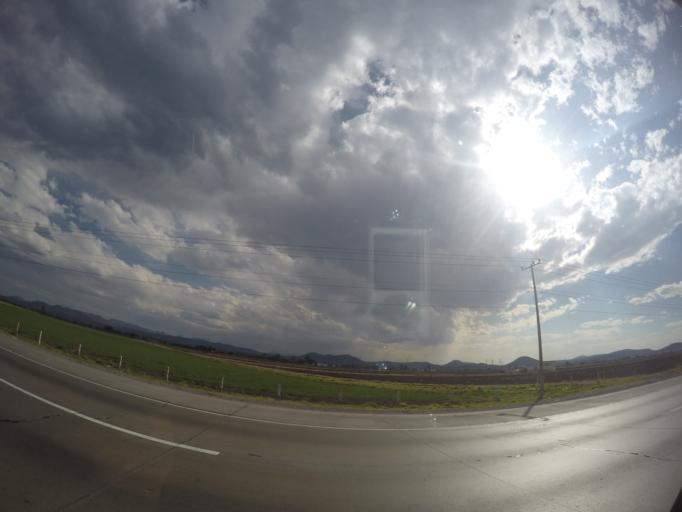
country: MX
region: Queretaro
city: El Sauz
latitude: 20.4564
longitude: -100.0905
